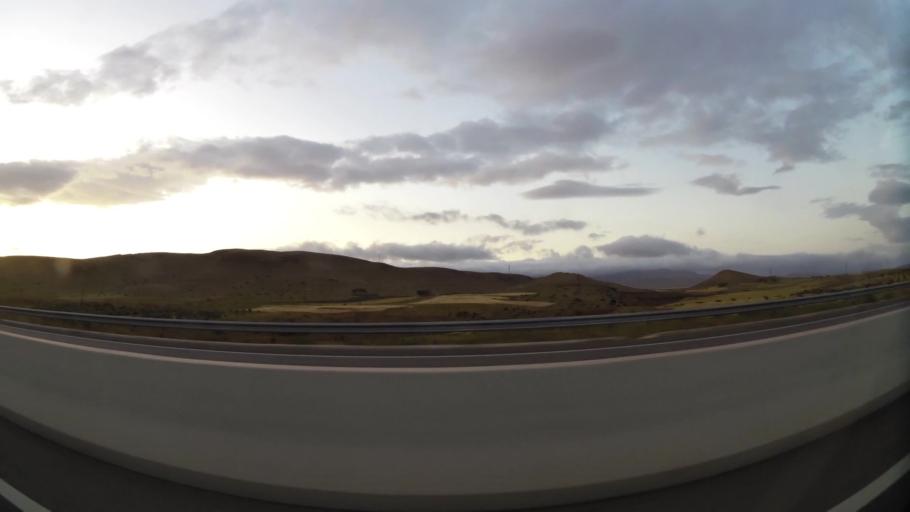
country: MA
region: Oriental
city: El Aioun
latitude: 34.6086
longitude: -2.5661
